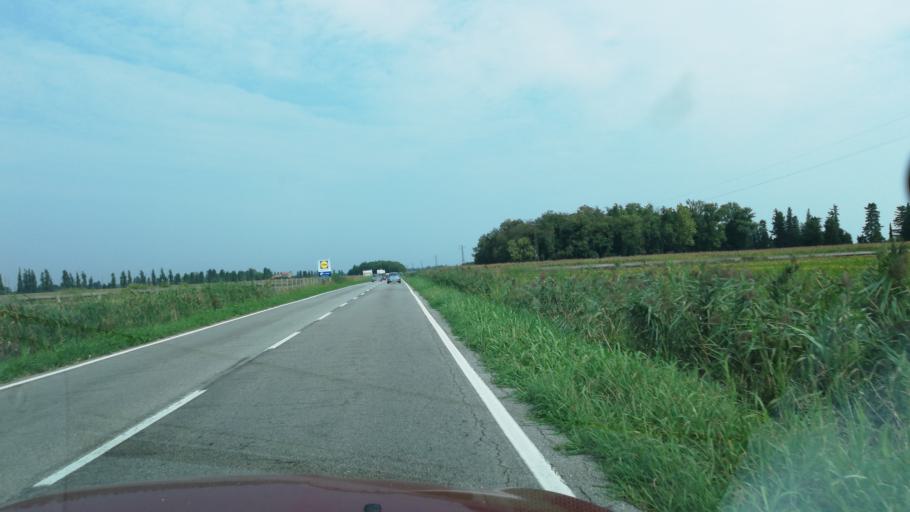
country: IT
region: Veneto
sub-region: Provincia di Venezia
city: La Salute di Livenza
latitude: 45.6121
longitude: 12.8027
